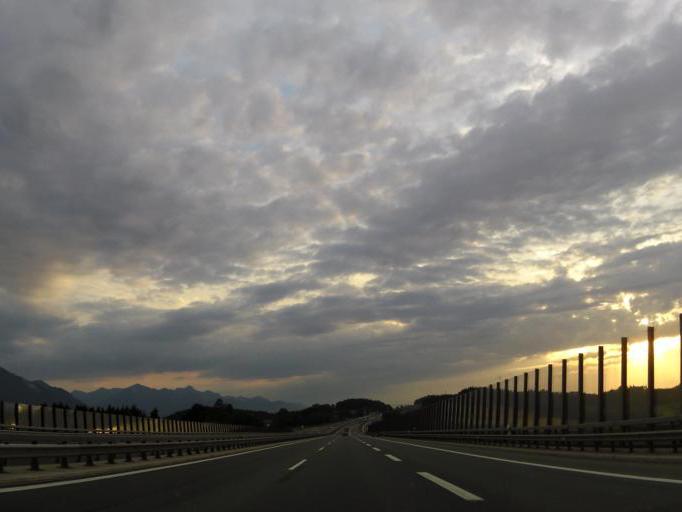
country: DE
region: Bavaria
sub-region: Upper Bavaria
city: Vachendorf
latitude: 47.8287
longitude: 12.6043
